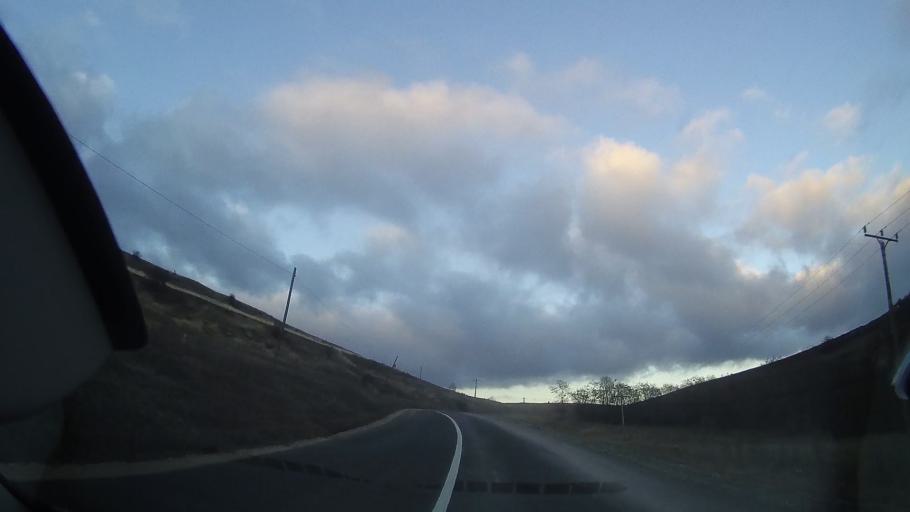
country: RO
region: Cluj
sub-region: Comuna Izvoru Crisului
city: Izvoru Crisului
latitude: 46.8105
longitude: 23.1214
